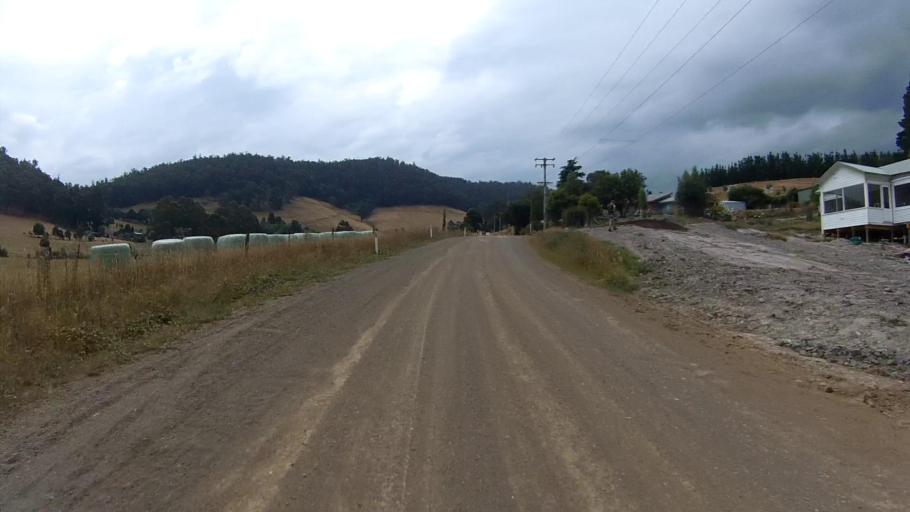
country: AU
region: Tasmania
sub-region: Huon Valley
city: Huonville
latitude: -42.9749
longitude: 147.0544
